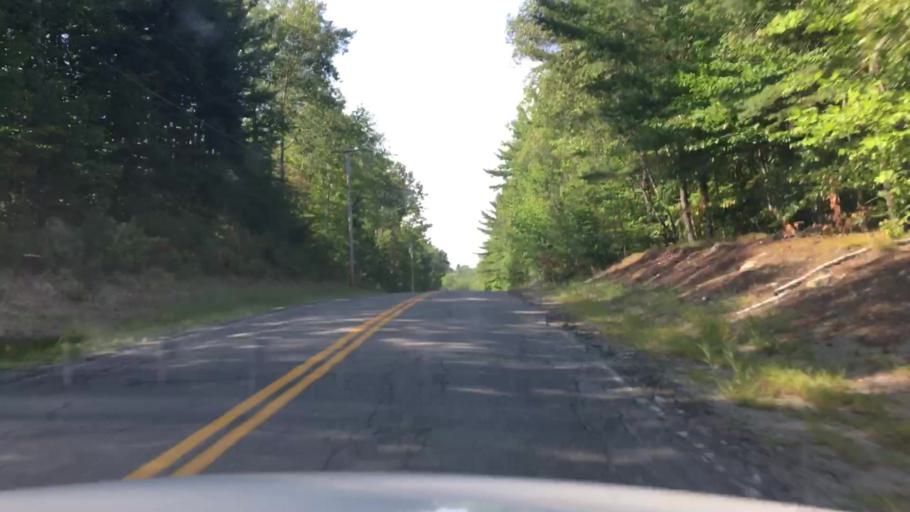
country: US
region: Maine
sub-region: Penobscot County
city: Enfield
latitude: 45.2105
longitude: -68.5234
